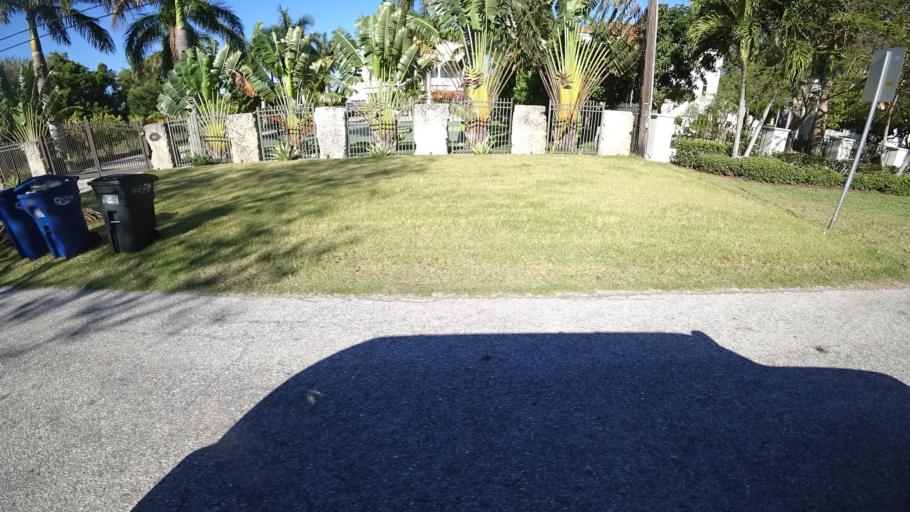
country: US
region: Florida
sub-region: Manatee County
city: West Bradenton
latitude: 27.4947
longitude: -82.6436
